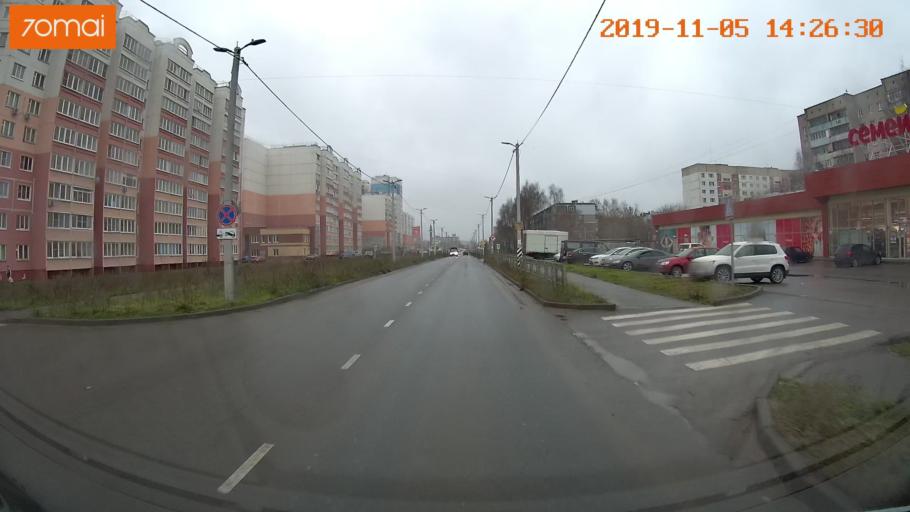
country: RU
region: Ivanovo
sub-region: Gorod Ivanovo
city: Ivanovo
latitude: 56.9702
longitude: 40.9850
